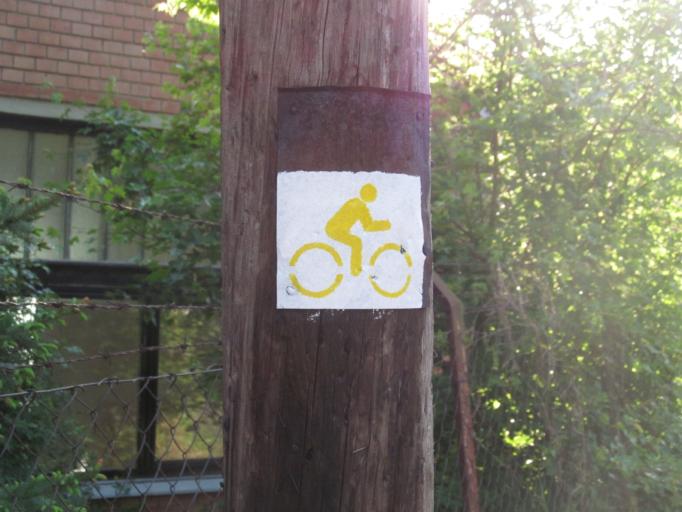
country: HU
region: Borsod-Abauj-Zemplen
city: Gonc
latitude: 48.5330
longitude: 21.4210
